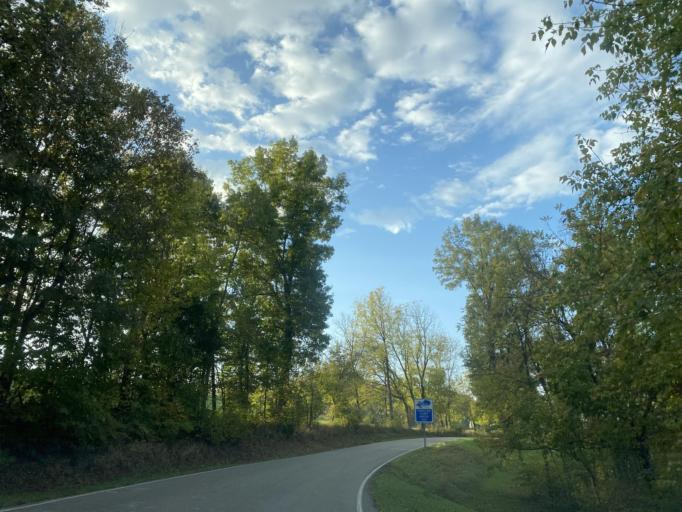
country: US
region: Kentucky
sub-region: Pendleton County
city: Falmouth
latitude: 38.7808
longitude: -84.3325
